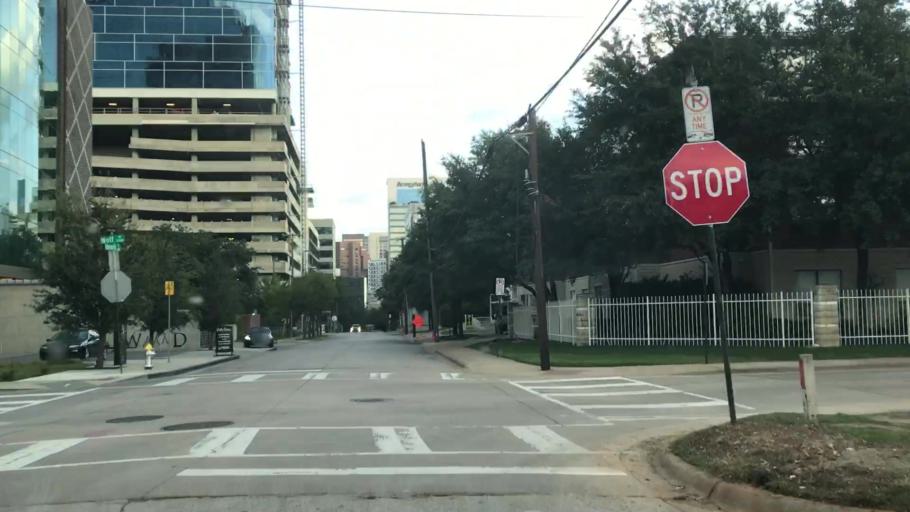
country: US
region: Texas
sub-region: Dallas County
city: Dallas
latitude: 32.7957
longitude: -96.8103
